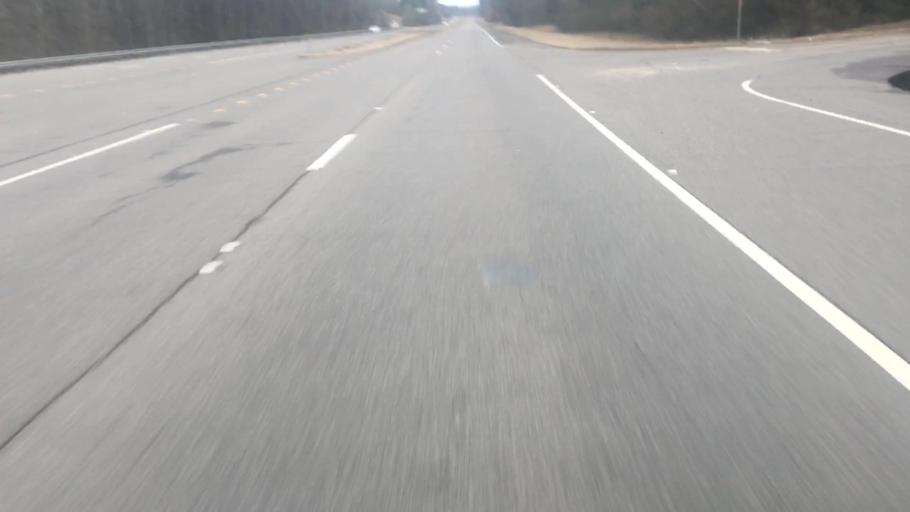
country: US
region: Alabama
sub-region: Walker County
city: Cordova
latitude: 33.8212
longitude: -87.1814
